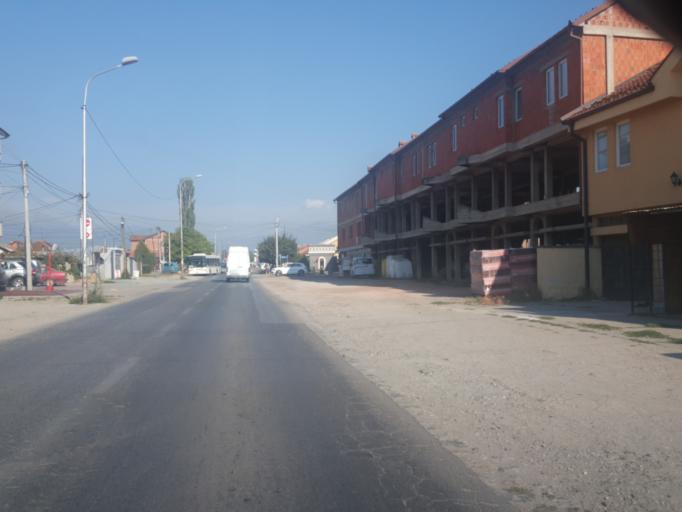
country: XK
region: Gjakova
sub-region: Komuna e Gjakoves
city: Gjakove
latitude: 42.4007
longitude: 20.4154
